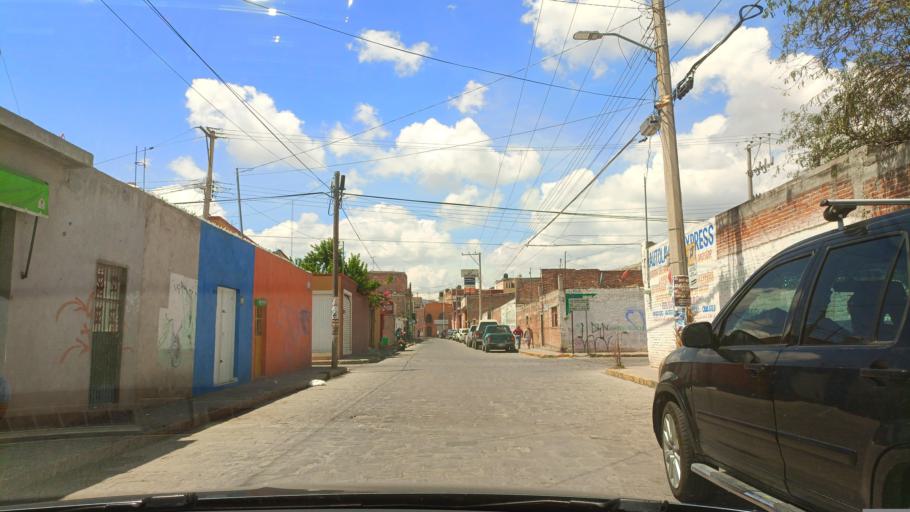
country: MX
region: Guerrero
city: San Luis de la Paz
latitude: 21.2985
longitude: -100.5223
